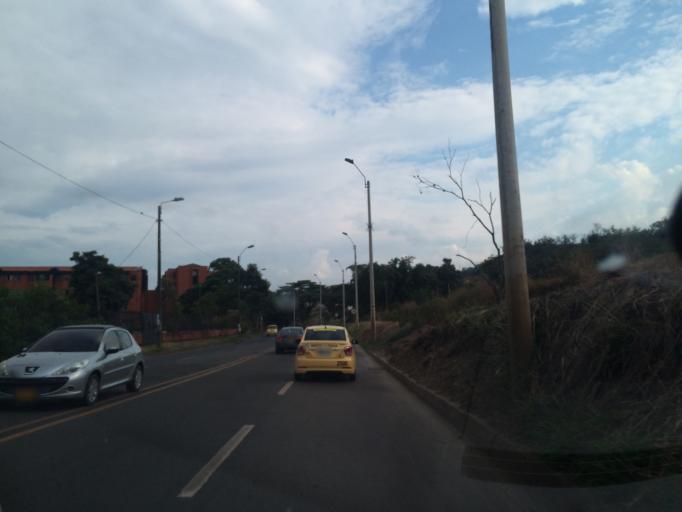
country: CO
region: Valle del Cauca
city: Cali
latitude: 3.4016
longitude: -76.5567
